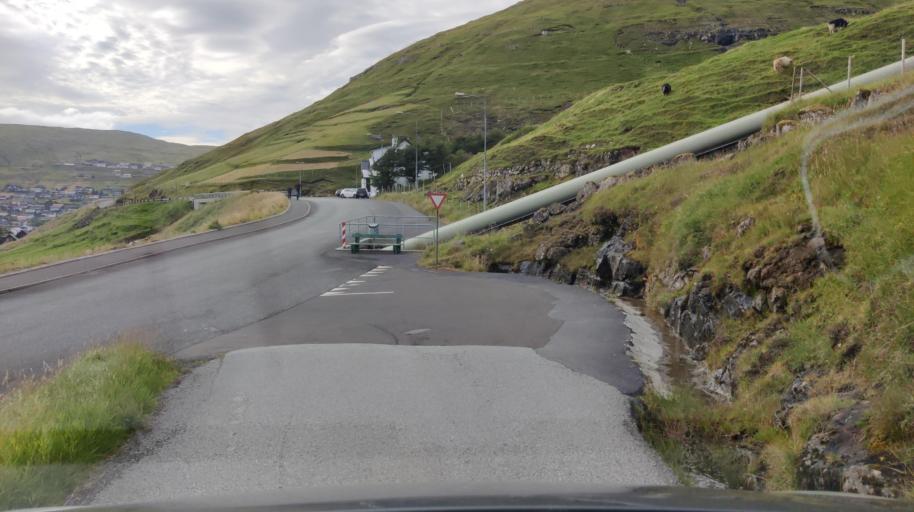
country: FO
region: Streymoy
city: Vestmanna
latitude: 62.1553
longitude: -7.1475
